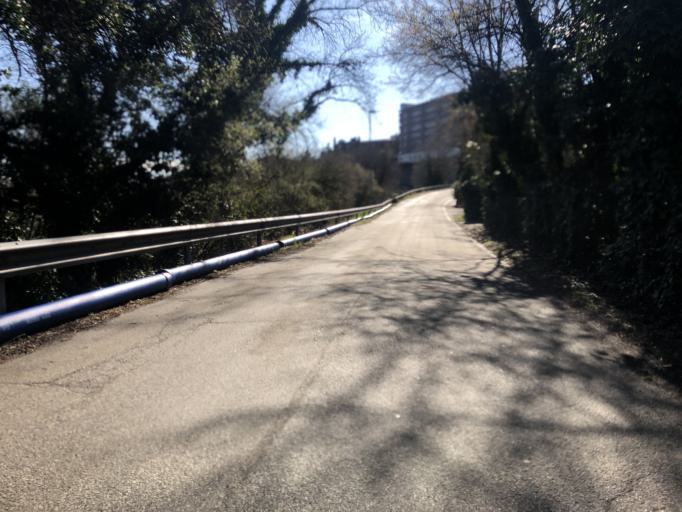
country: IT
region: Veneto
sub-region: Provincia di Verona
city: Bussolengo
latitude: 45.4781
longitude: 10.8470
